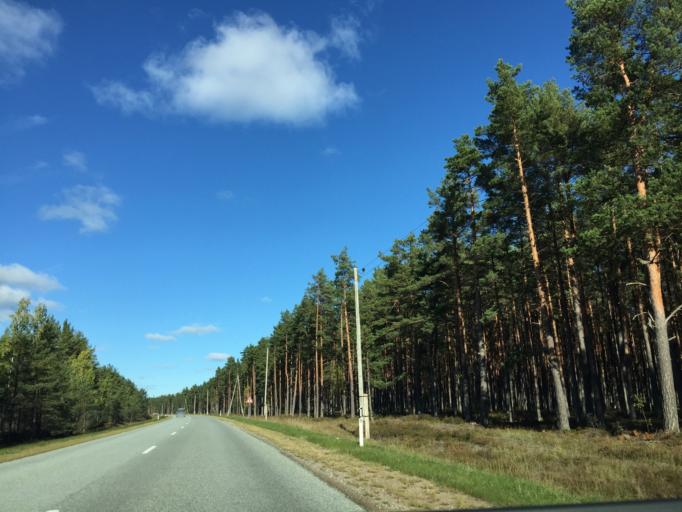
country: LV
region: Mesraga
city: Mersrags
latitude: 57.2590
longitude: 23.1727
